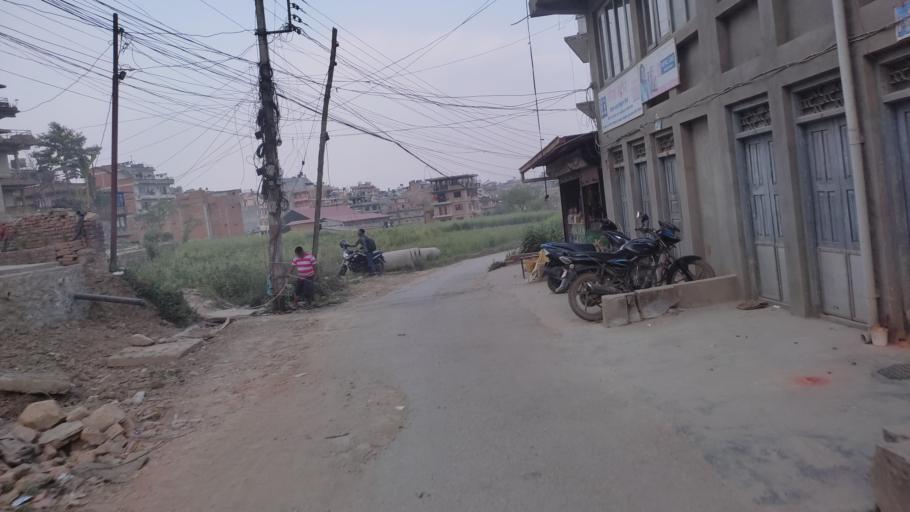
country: NP
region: Central Region
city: Kirtipur
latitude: 27.6665
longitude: 85.2774
